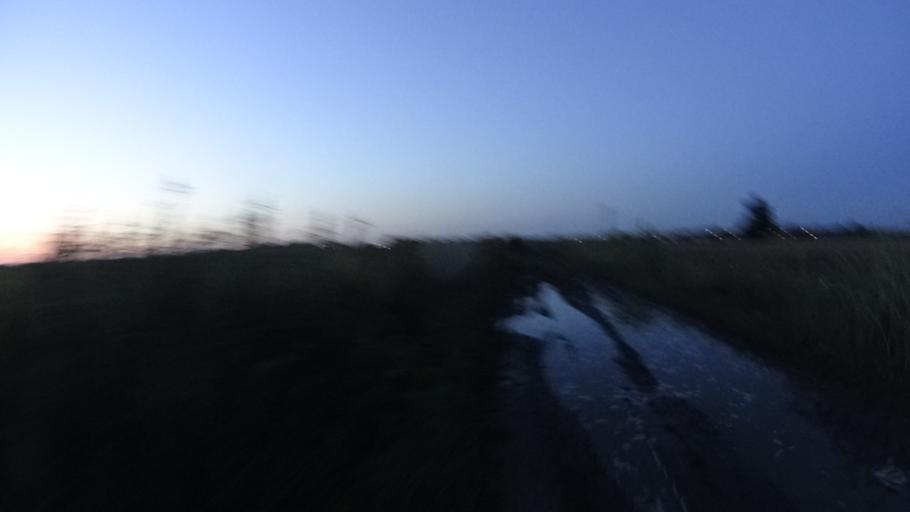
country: PL
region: Masovian Voivodeship
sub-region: Powiat warszawski zachodni
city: Ozarow Mazowiecki
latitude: 52.2244
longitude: 20.7912
